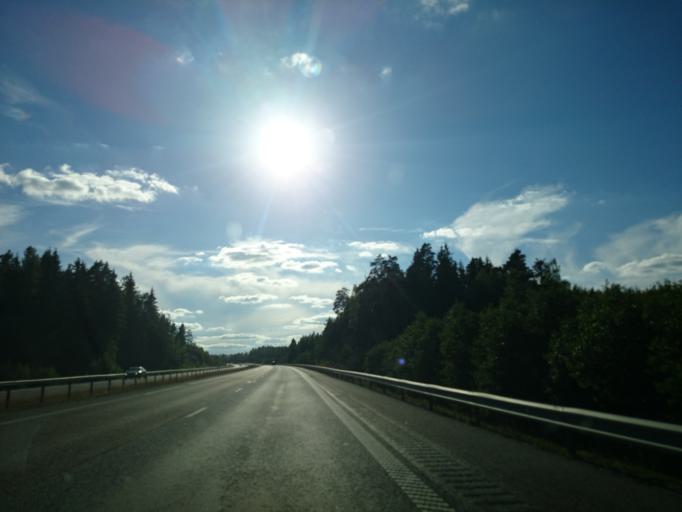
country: SE
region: Soedermanland
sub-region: Nykopings Kommun
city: Olstorp
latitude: 58.7552
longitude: 16.5708
